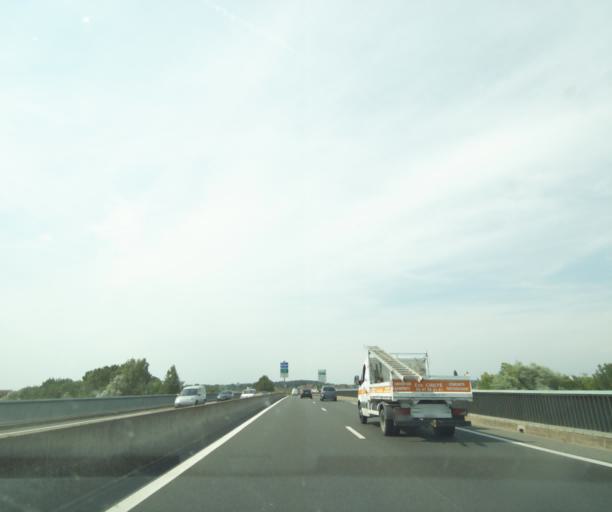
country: FR
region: Centre
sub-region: Departement d'Indre-et-Loire
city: La Riche
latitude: 47.3744
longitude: 0.6525
